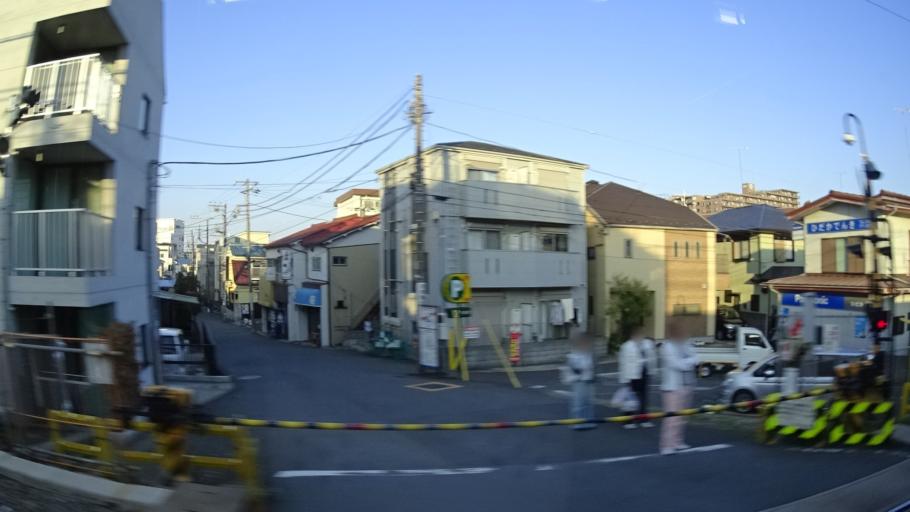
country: JP
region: Kanagawa
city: Yokohama
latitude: 35.3821
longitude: 139.6166
